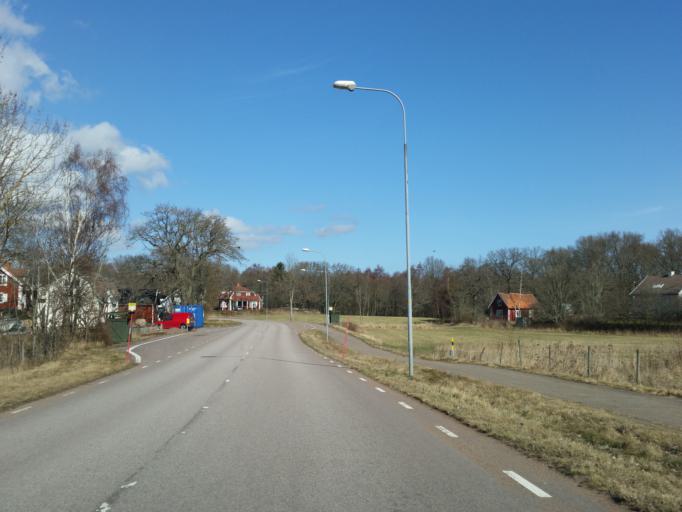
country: SE
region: Kalmar
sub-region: Monsteras Kommun
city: Timmernabben
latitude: 56.9060
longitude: 16.4335
